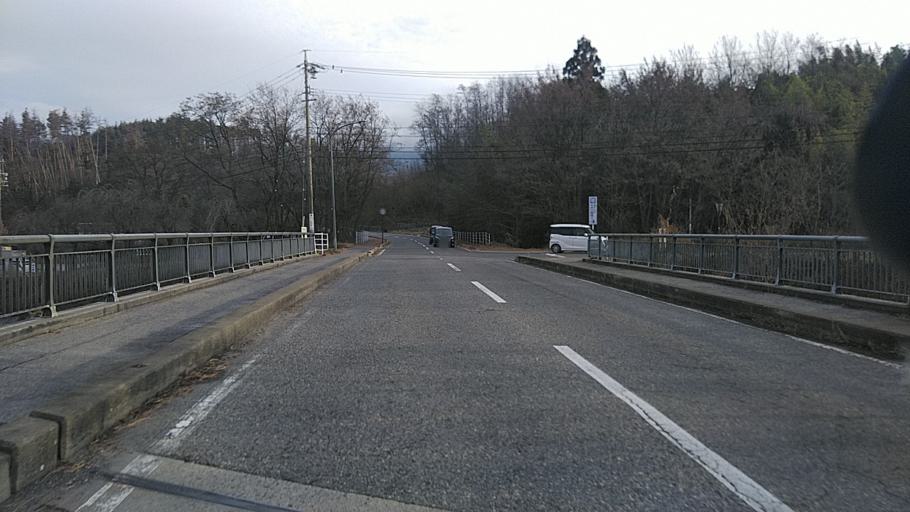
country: JP
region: Nagano
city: Matsumoto
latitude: 36.1832
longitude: 137.9921
